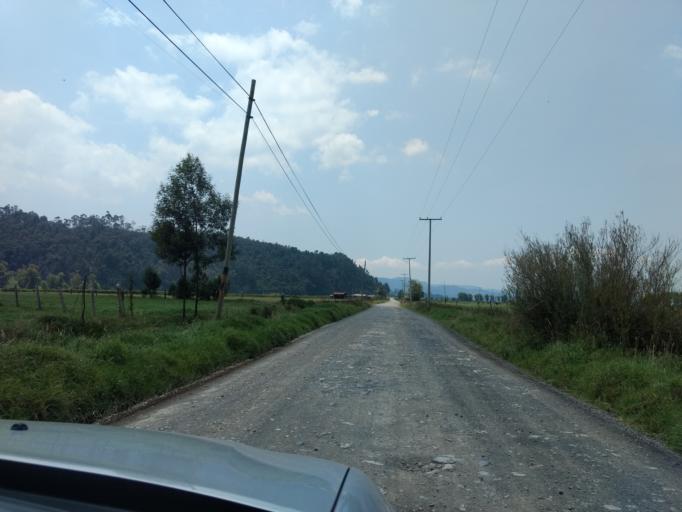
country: CO
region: Boyaca
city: Raquira
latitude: 5.4994
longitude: -73.7112
